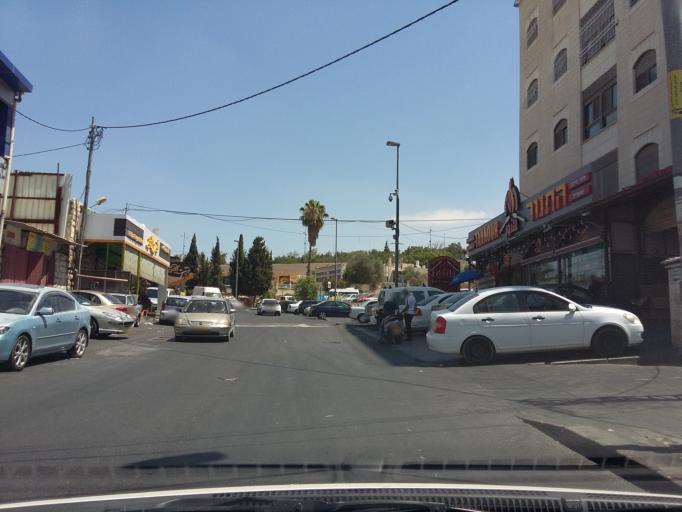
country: PS
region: West Bank
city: East Jerusalem
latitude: 31.7923
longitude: 35.2368
